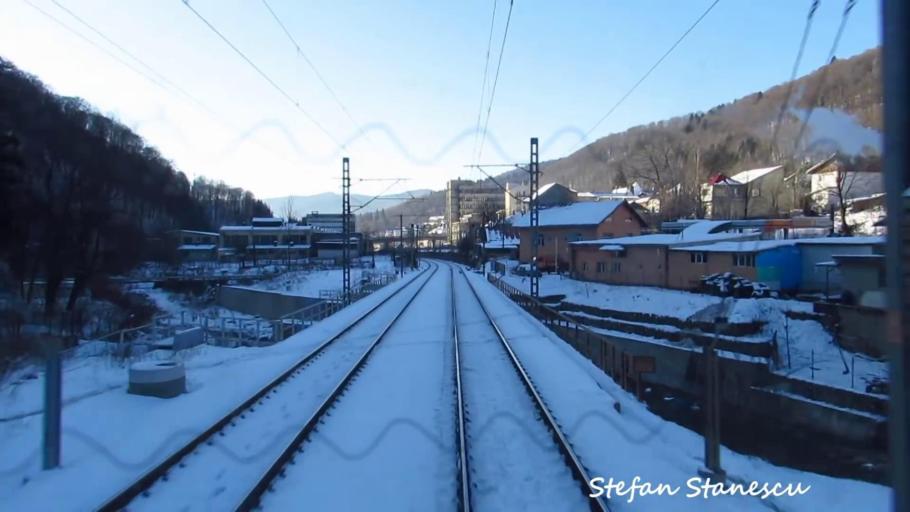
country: RO
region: Prahova
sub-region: Oras Sinaia
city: Sinaia
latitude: 45.3442
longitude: 25.5508
